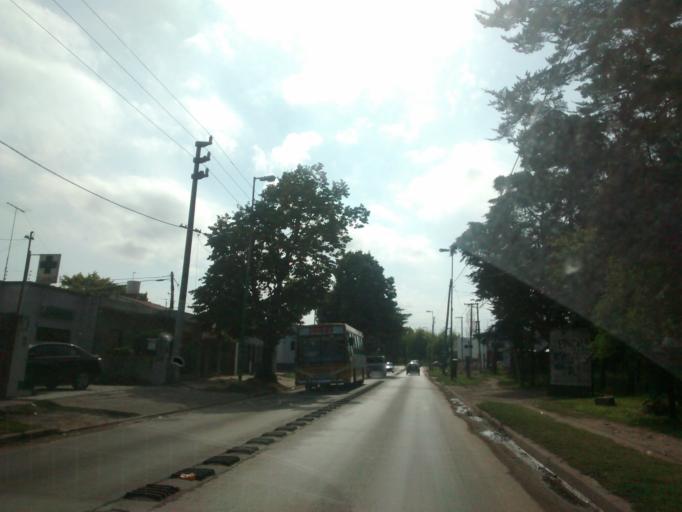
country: AR
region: Buenos Aires
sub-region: Partido de La Plata
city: La Plata
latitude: -34.9457
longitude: -57.9092
